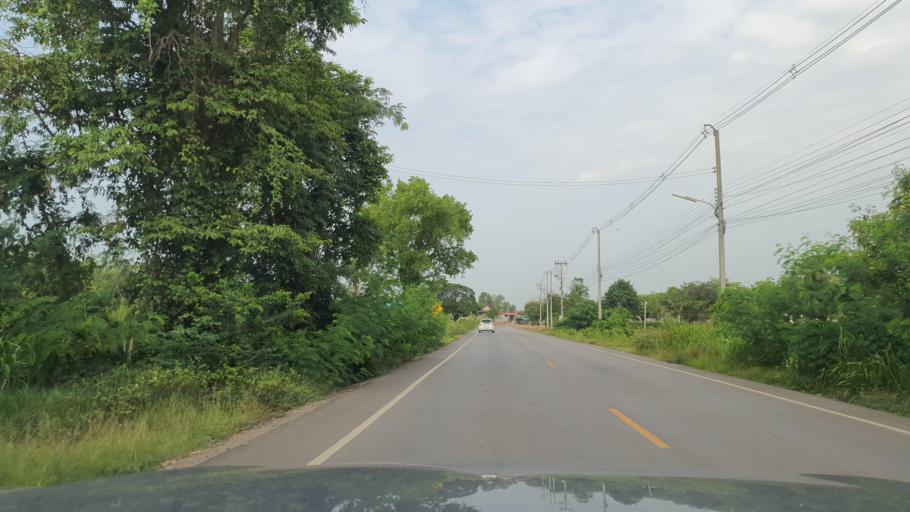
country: TH
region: Phitsanulok
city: Phitsanulok
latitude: 16.8152
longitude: 100.1945
